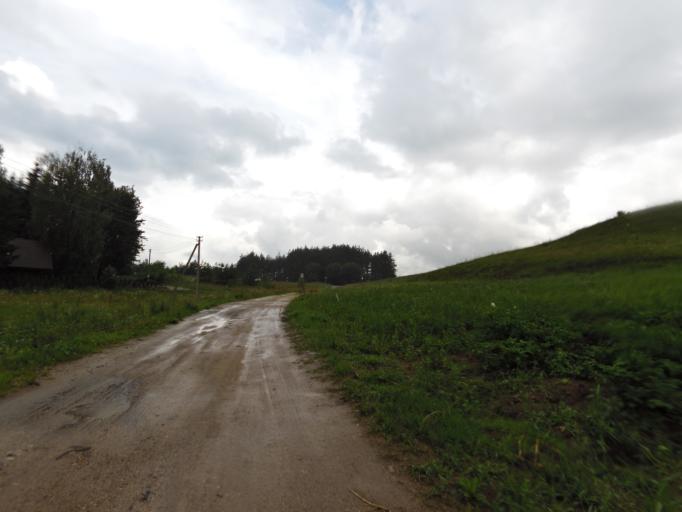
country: LT
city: Grigiskes
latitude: 54.7164
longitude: 25.1145
